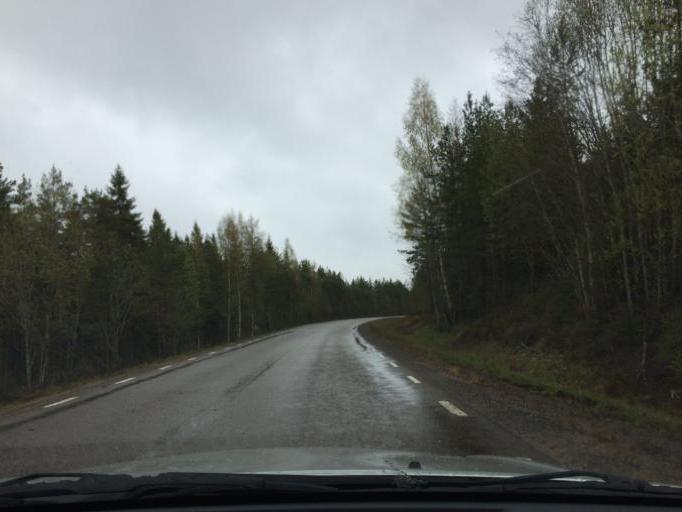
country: SE
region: Dalarna
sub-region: Ludvika Kommun
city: Abborrberget
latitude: 60.0633
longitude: 14.8116
